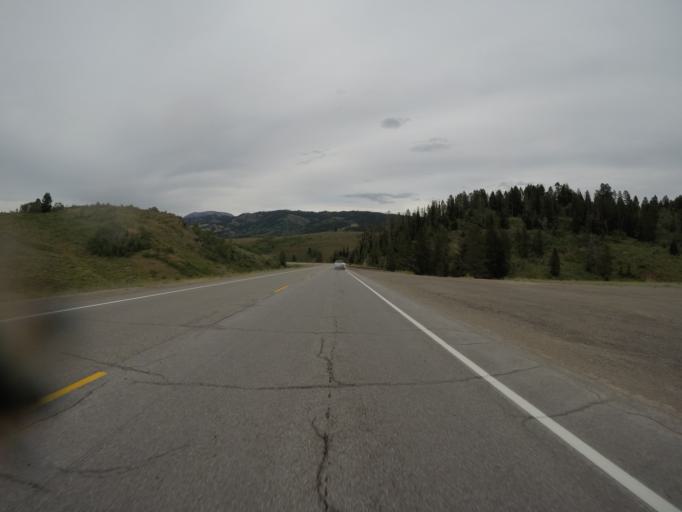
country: US
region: Wyoming
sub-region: Lincoln County
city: Afton
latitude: 42.5186
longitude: -110.9004
